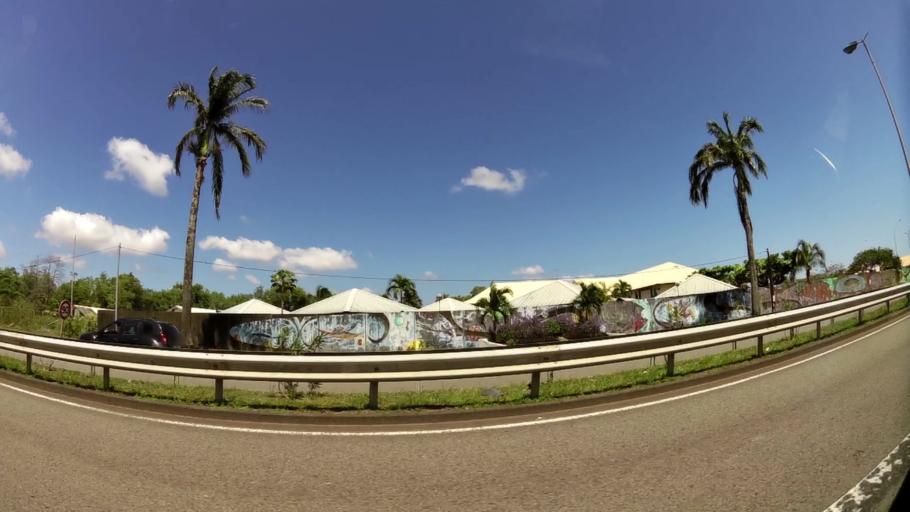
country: GF
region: Guyane
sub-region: Guyane
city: Cayenne
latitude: 4.9306
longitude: -52.3298
